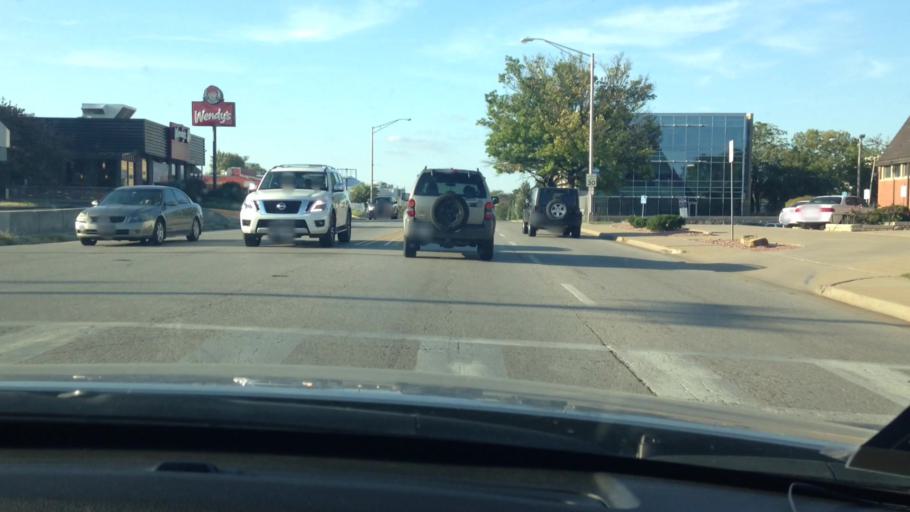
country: US
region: Kansas
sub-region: Johnson County
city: Westwood
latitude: 39.0513
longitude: -94.6118
